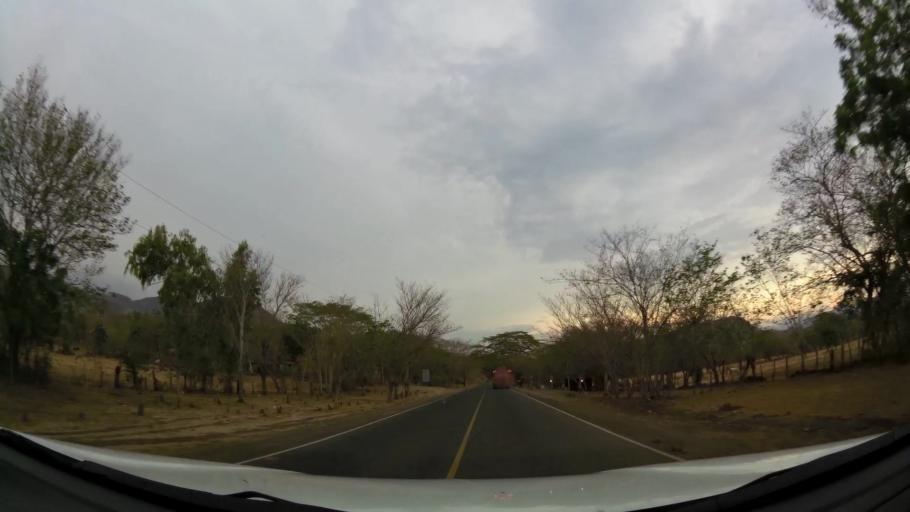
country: NI
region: Leon
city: La Jicaral
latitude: 12.7155
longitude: -86.3949
